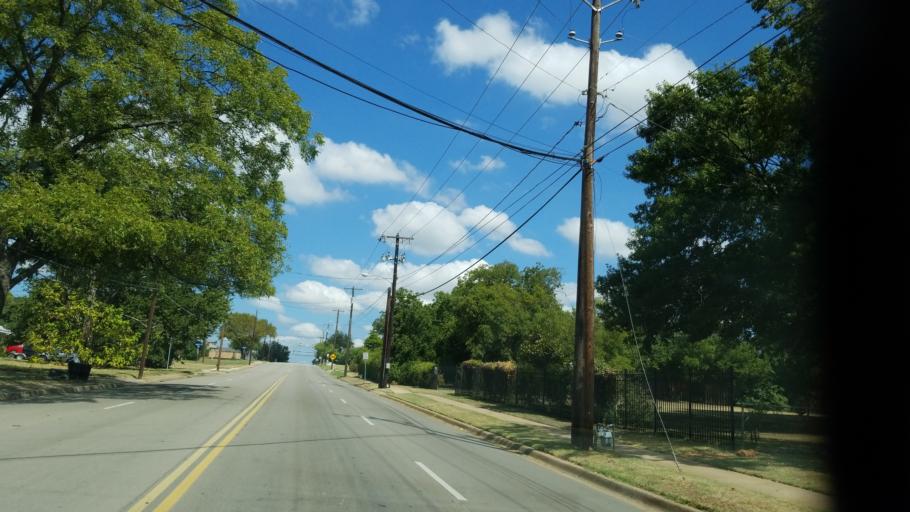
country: US
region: Texas
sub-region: Tarrant County
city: Euless
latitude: 32.8331
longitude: -97.0825
